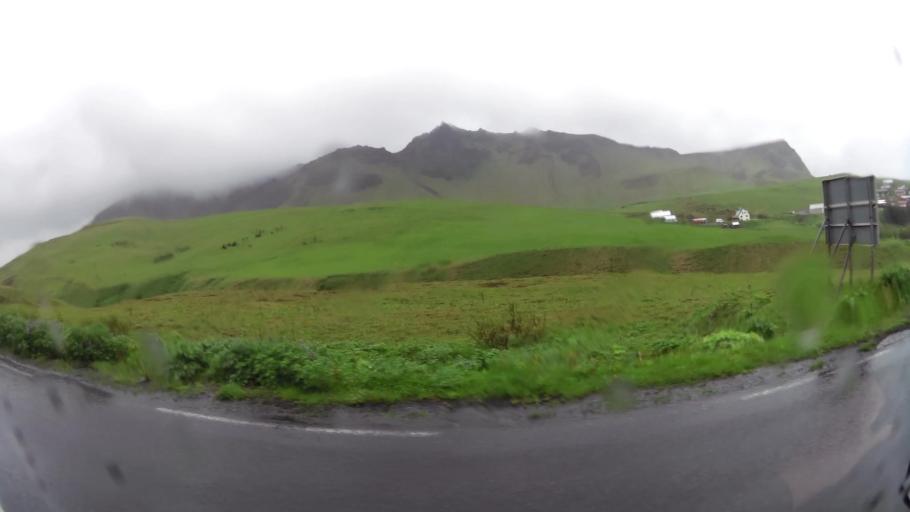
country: IS
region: South
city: Vestmannaeyjar
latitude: 63.4230
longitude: -19.0158
